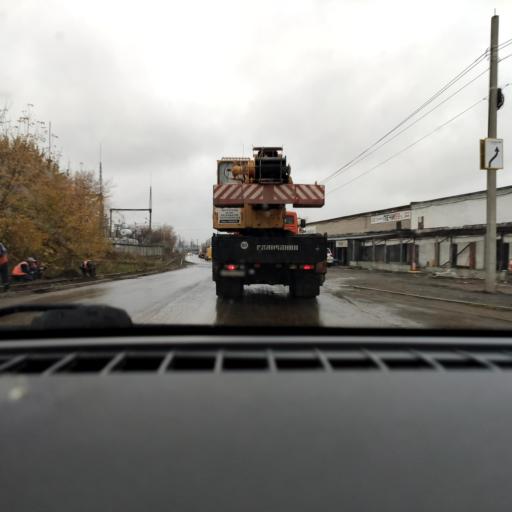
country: RU
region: Perm
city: Froly
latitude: 57.9527
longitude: 56.2525
